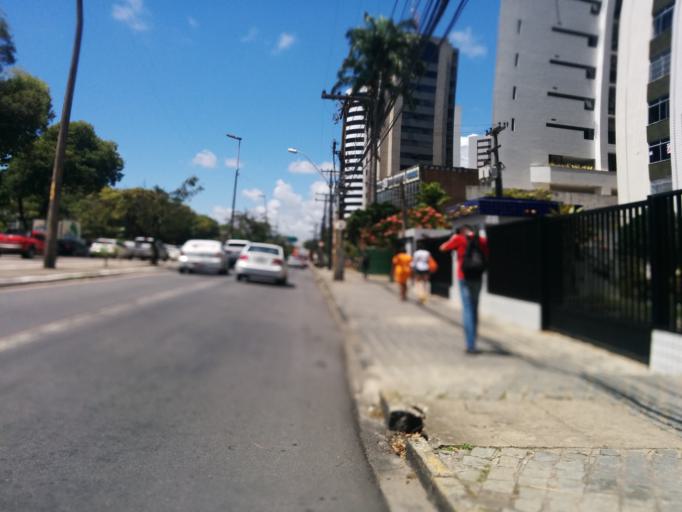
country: BR
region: Pernambuco
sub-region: Recife
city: Recife
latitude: -8.0474
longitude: -34.8924
